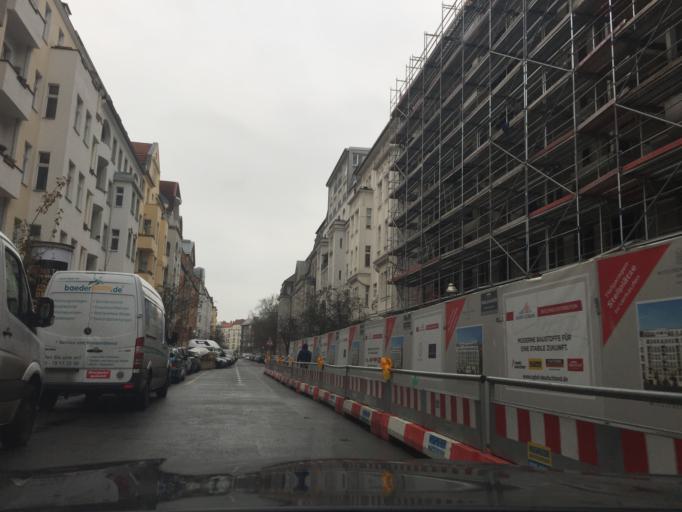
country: DE
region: Berlin
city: Charlottenburg Bezirk
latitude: 52.5104
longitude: 13.2955
